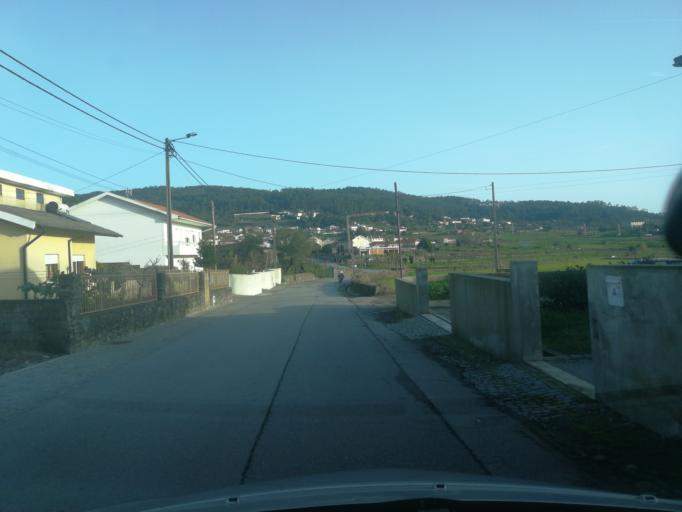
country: PT
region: Braga
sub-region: Barcelos
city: Galegos
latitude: 41.5185
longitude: -8.5701
